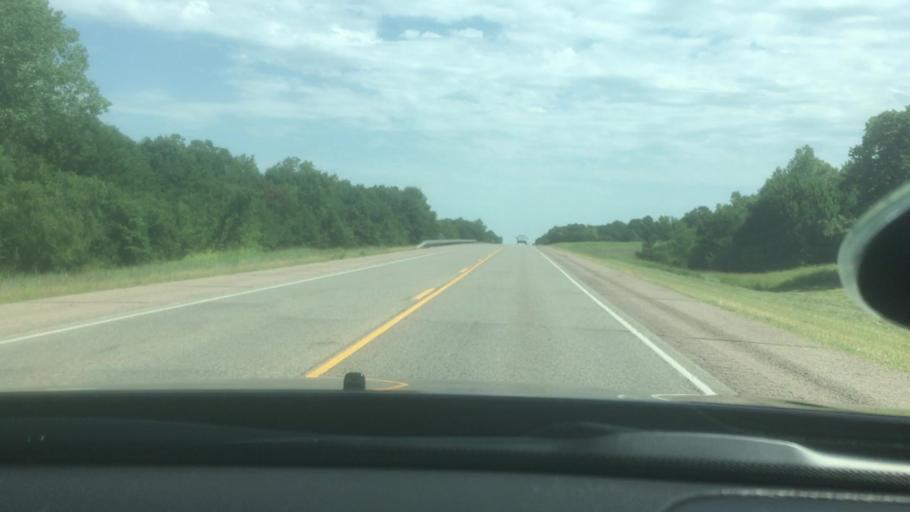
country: US
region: Oklahoma
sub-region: Seminole County
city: Konawa
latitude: 35.0067
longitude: -96.9314
